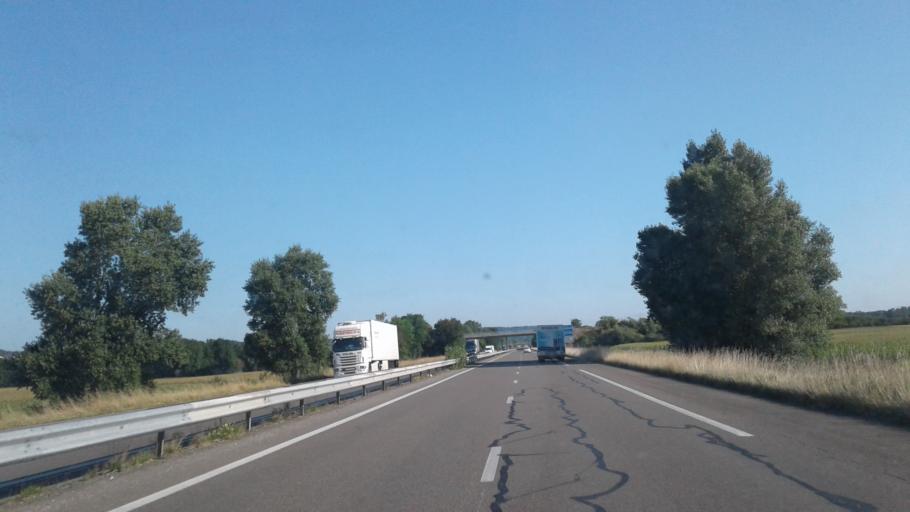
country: FR
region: Rhone-Alpes
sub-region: Departement de l'Ain
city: Chateau-Gaillard
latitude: 45.9974
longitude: 5.3131
